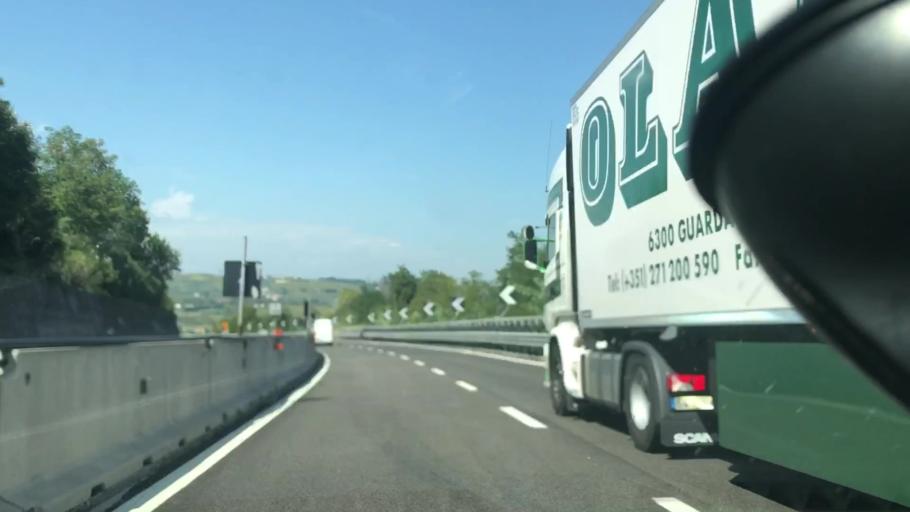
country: IT
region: Abruzzo
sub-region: Provincia di Chieti
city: Tollo
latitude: 42.3712
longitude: 14.3155
